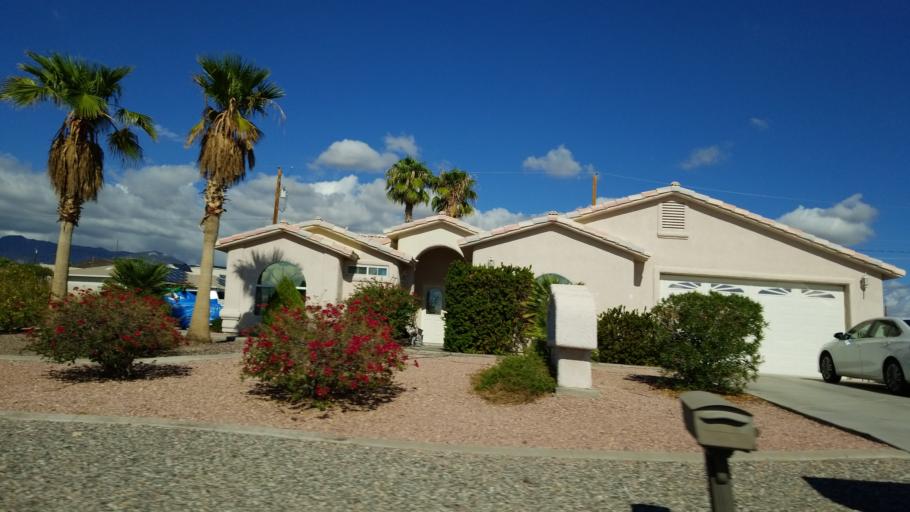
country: US
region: Arizona
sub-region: Mohave County
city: Lake Havasu City
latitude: 34.4753
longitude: -114.2660
